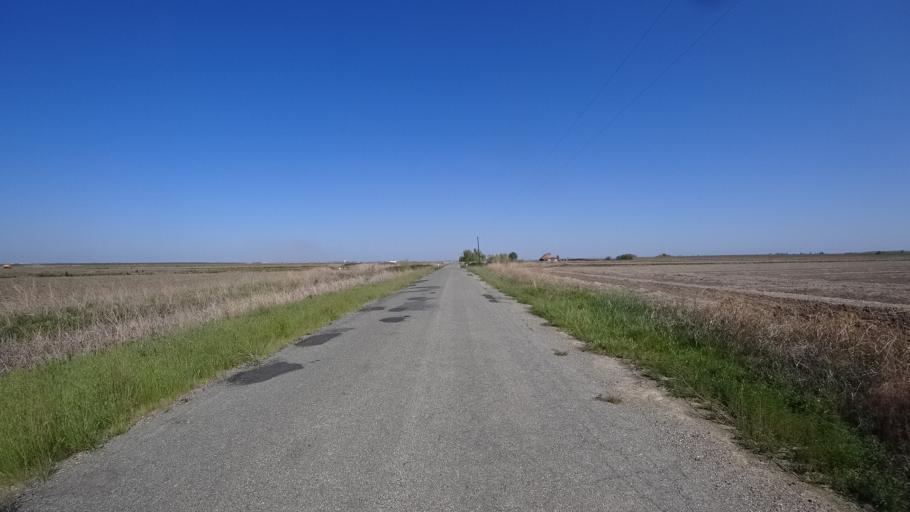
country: US
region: California
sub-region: Glenn County
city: Willows
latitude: 39.5074
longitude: -122.0373
